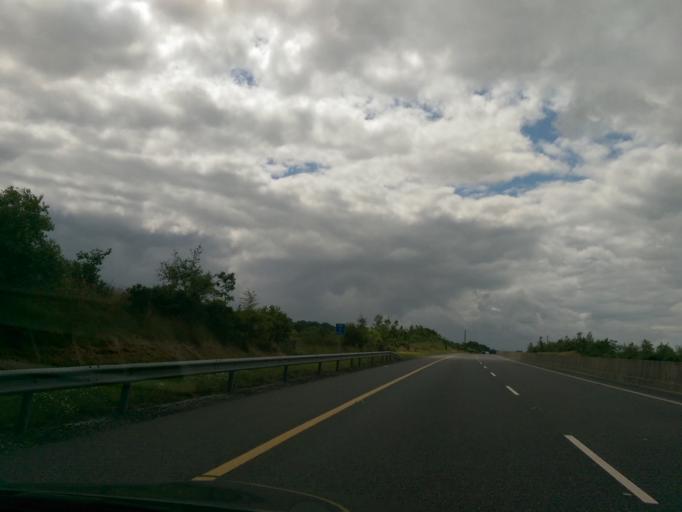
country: IE
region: Munster
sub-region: County Cork
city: Mitchelstown
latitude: 52.2533
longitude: -8.2570
